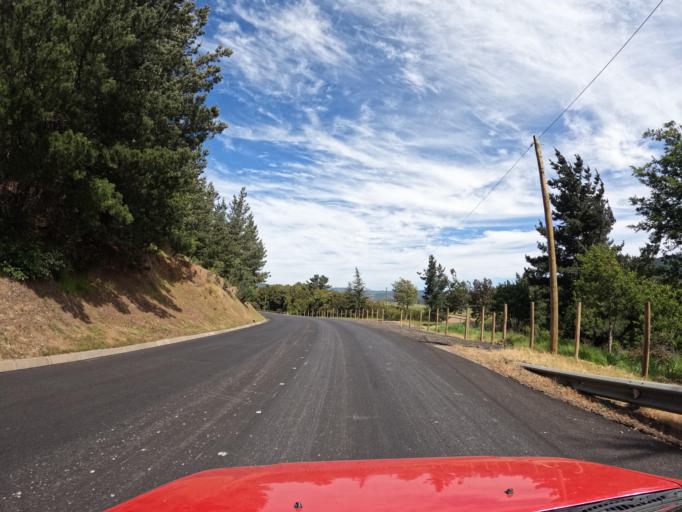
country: CL
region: Maule
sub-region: Provincia de Talca
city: Constitucion
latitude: -35.0430
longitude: -72.0594
